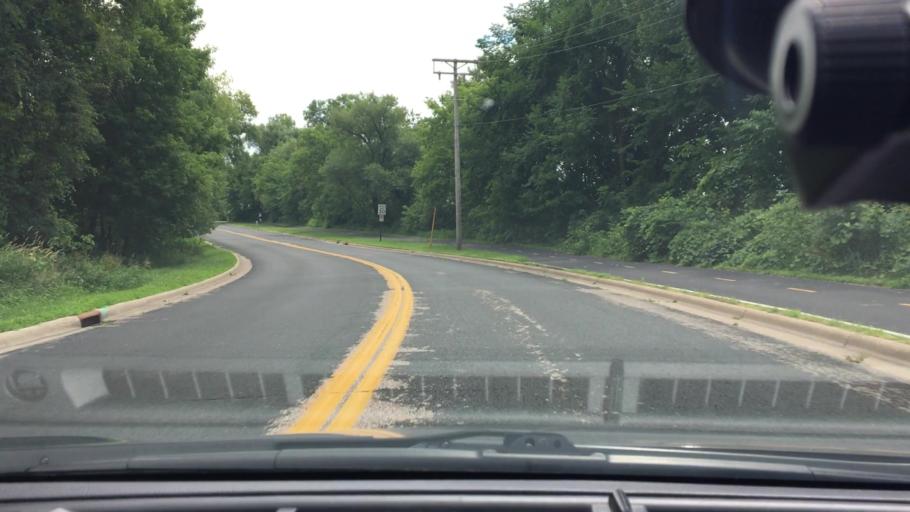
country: US
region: Minnesota
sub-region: Hennepin County
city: Plymouth
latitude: 45.0178
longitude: -93.4207
